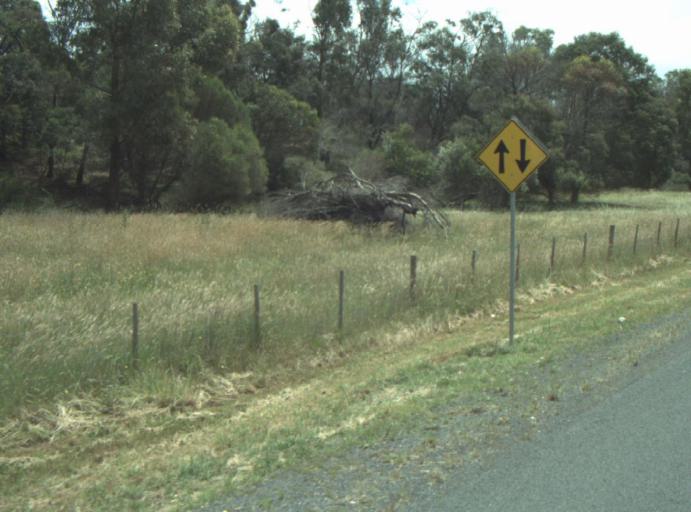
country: AU
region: Victoria
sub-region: Greater Geelong
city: Wandana Heights
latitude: -38.2373
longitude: 144.2789
